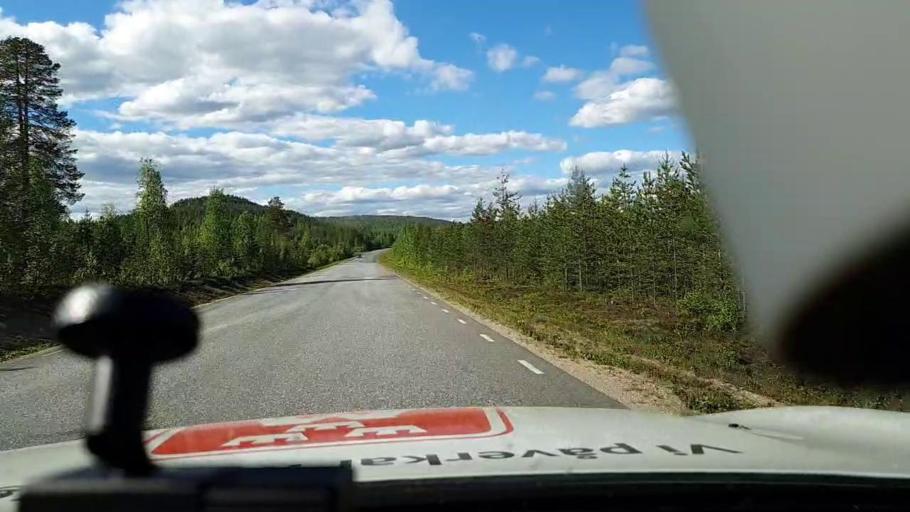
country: FI
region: Lapland
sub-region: Torniolaakso
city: Ylitornio
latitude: 66.3004
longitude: 23.6327
